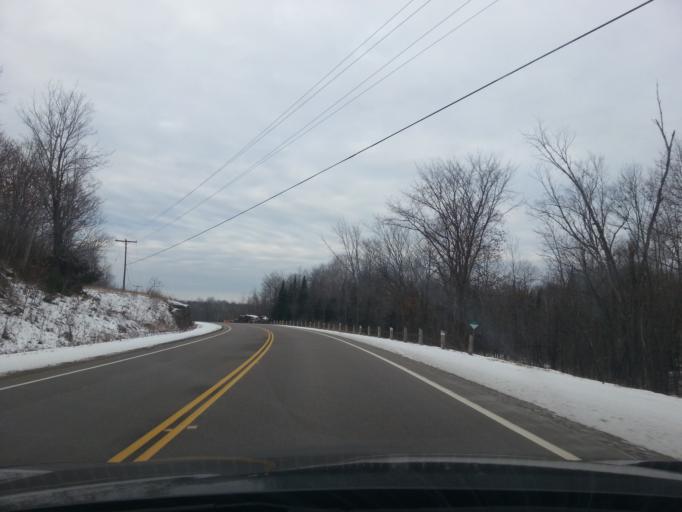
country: CA
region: Ontario
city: Skatepark
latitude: 44.7535
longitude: -76.9096
